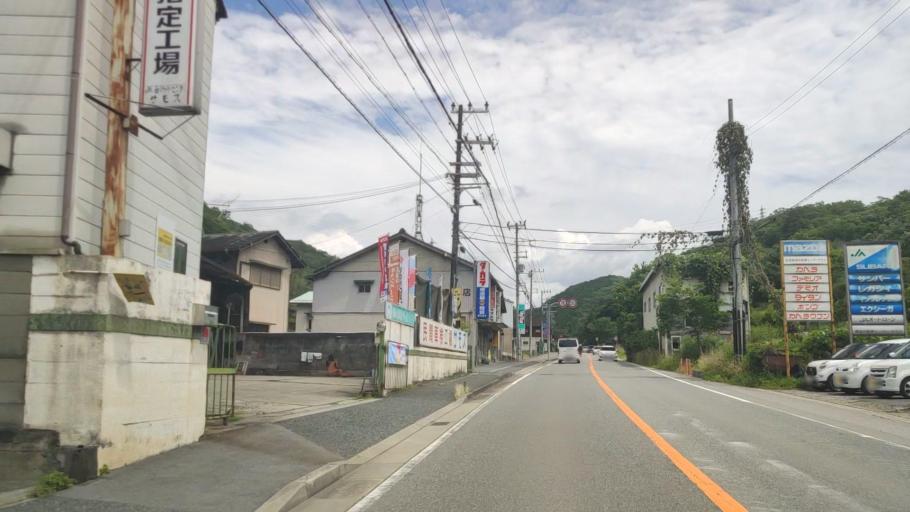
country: JP
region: Hyogo
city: Yamazakicho-nakabirose
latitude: 35.0042
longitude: 134.3663
